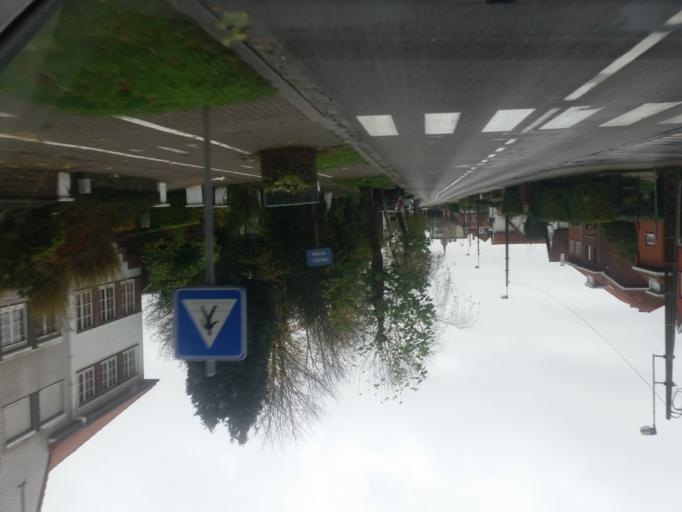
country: BE
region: Flanders
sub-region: Provincie Vlaams-Brabant
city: Grimbergen
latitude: 50.9166
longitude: 4.3603
